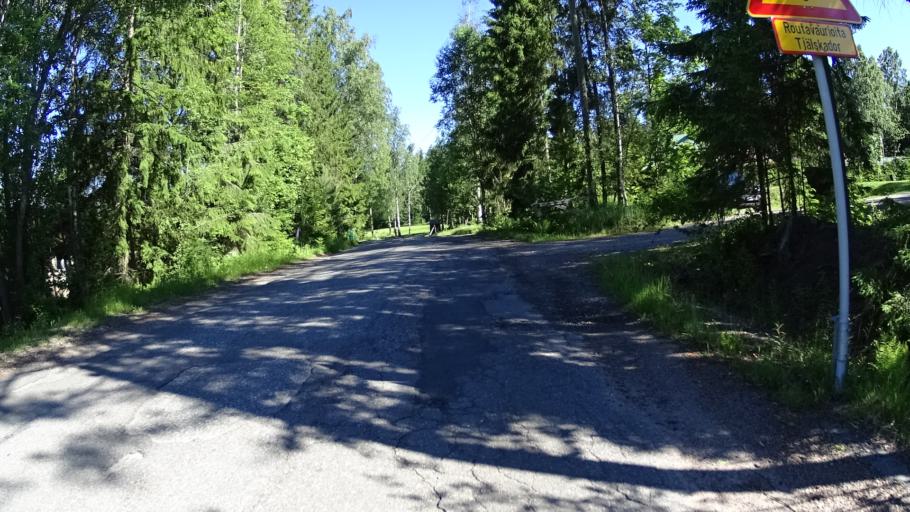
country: FI
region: Uusimaa
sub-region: Helsinki
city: Kilo
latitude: 60.3236
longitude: 24.8088
